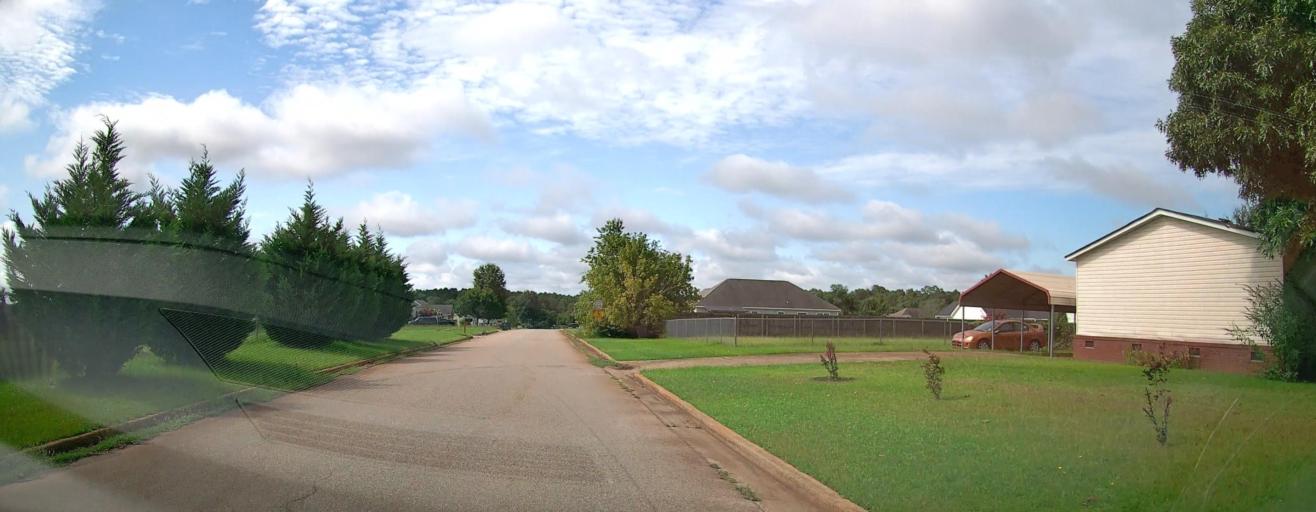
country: US
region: Georgia
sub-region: Houston County
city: Centerville
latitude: 32.6482
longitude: -83.7204
